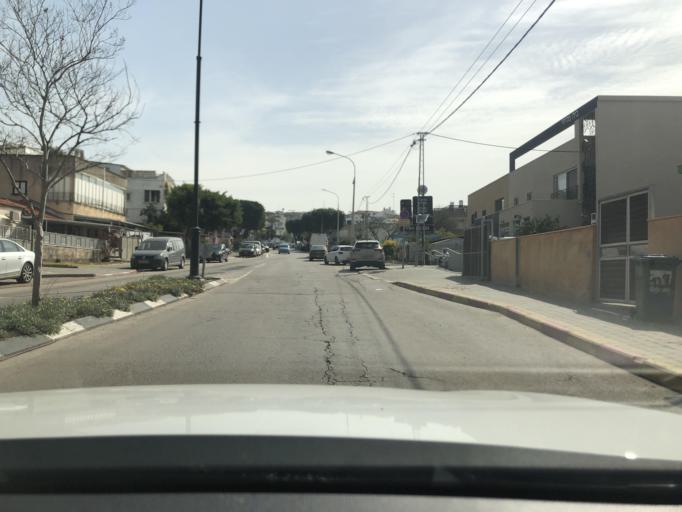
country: IL
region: Central District
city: Rosh Ha'Ayin
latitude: 32.0886
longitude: 34.9511
